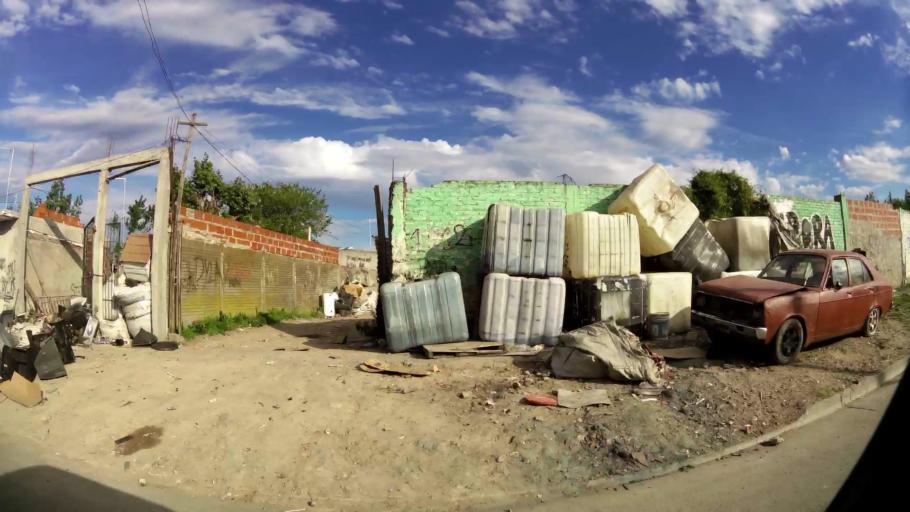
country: AR
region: Buenos Aires
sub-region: Partido de Lanus
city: Lanus
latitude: -34.7044
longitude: -58.3557
